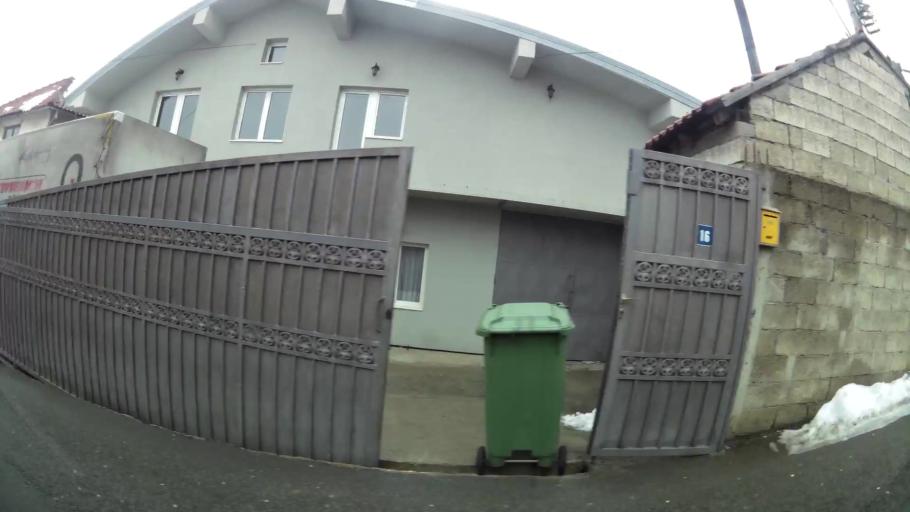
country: RS
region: Central Serbia
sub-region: Belgrade
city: Zvezdara
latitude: 44.7747
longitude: 20.5221
